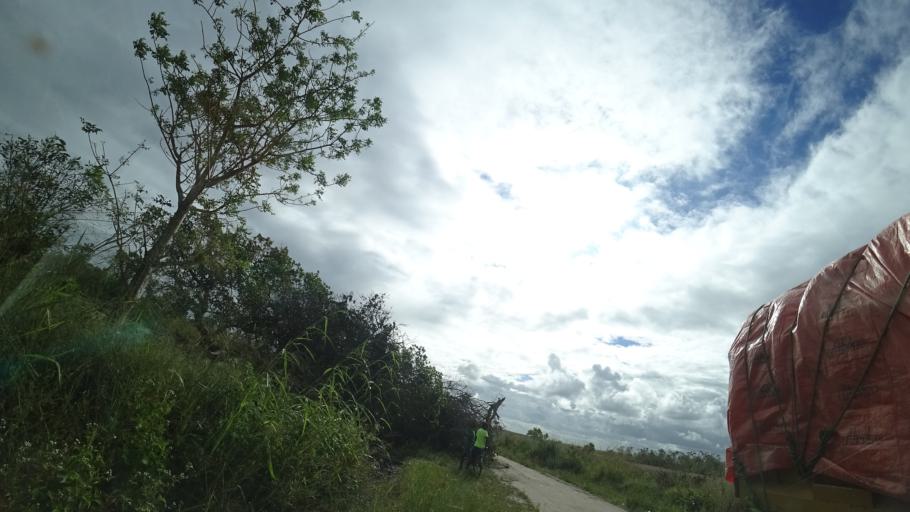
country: MZ
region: Sofala
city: Dondo
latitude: -19.5776
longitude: 35.1177
